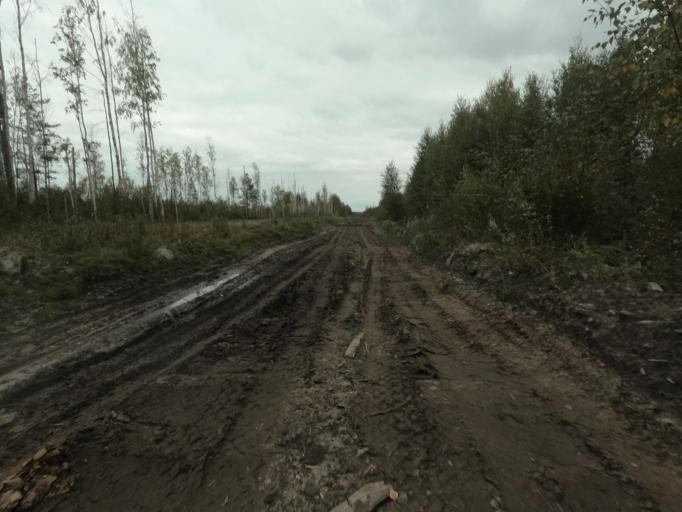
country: RU
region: St.-Petersburg
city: Sapernyy
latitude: 59.7576
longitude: 30.7103
